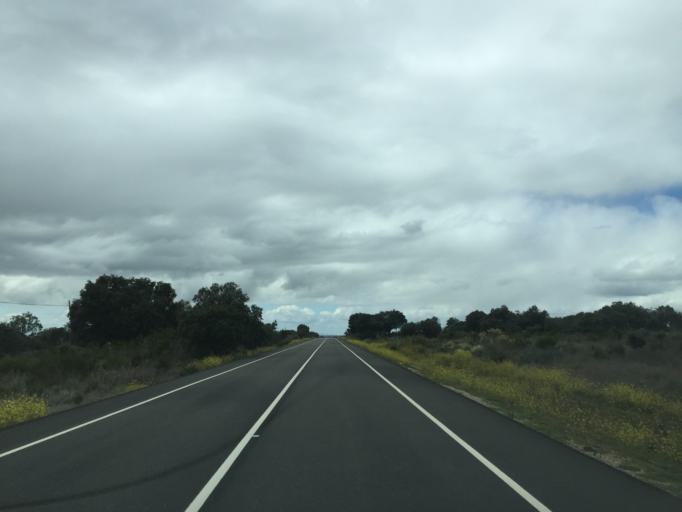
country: ES
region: Castille and Leon
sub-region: Provincia de Zamora
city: Torregamones
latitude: 41.4750
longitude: -6.2120
